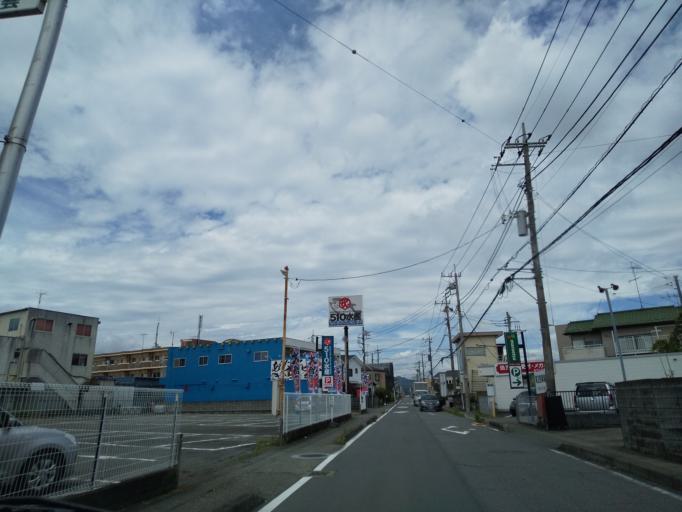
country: JP
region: Kanagawa
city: Zama
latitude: 35.5151
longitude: 139.3374
